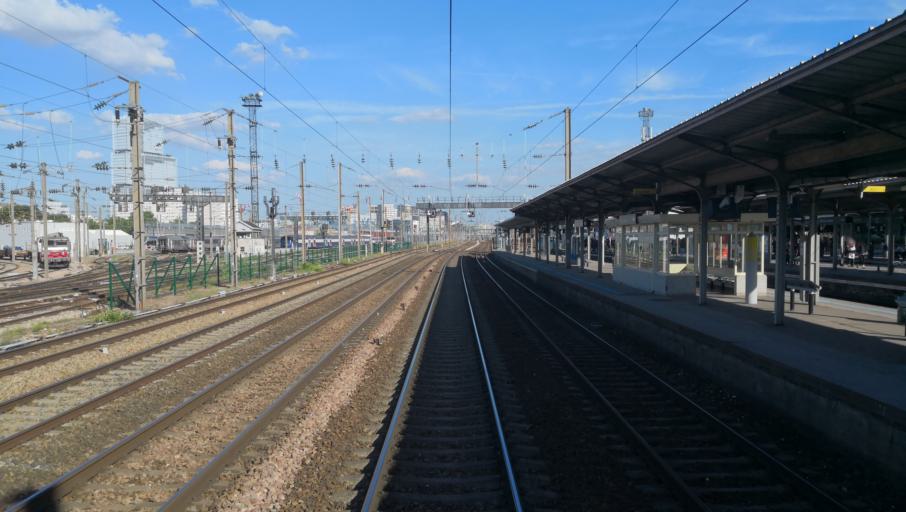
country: FR
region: Ile-de-France
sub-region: Departement des Hauts-de-Seine
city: Levallois-Perret
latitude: 48.8975
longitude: 2.2980
